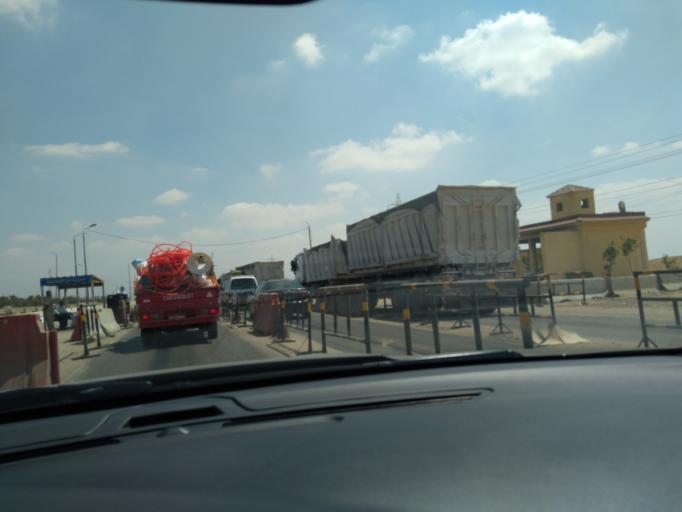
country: EG
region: Al Isma'iliyah
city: At Tall al Kabir
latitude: 30.4026
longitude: 31.9900
